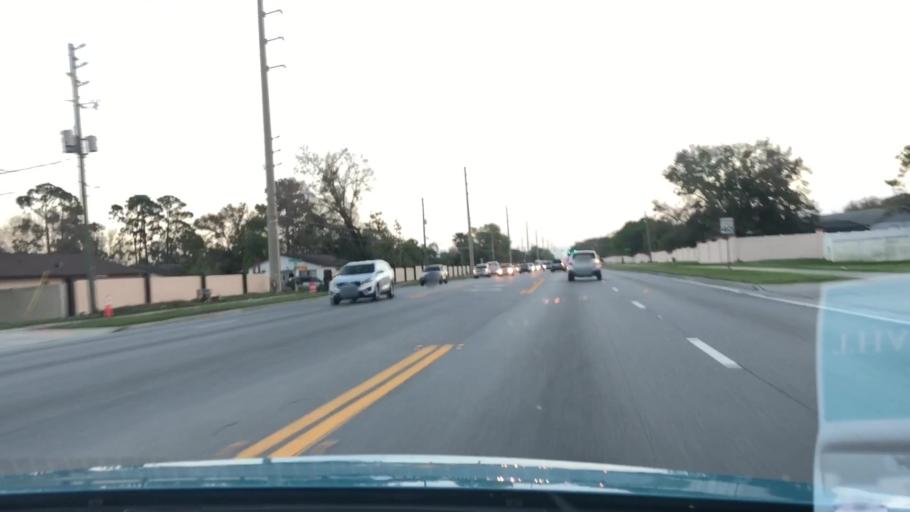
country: US
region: Florida
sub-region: Osceola County
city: Kissimmee
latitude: 28.3184
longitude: -81.3913
